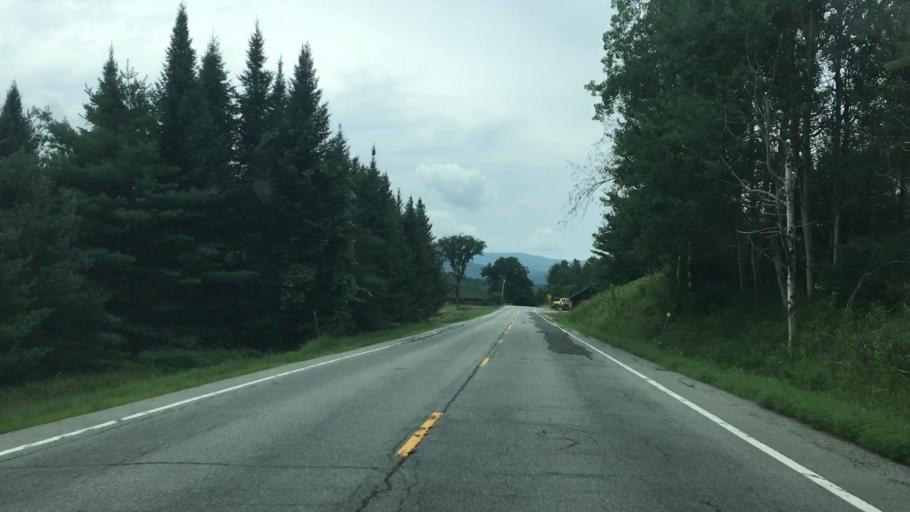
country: US
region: New York
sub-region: Essex County
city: Elizabethtown
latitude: 44.3917
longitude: -73.7099
